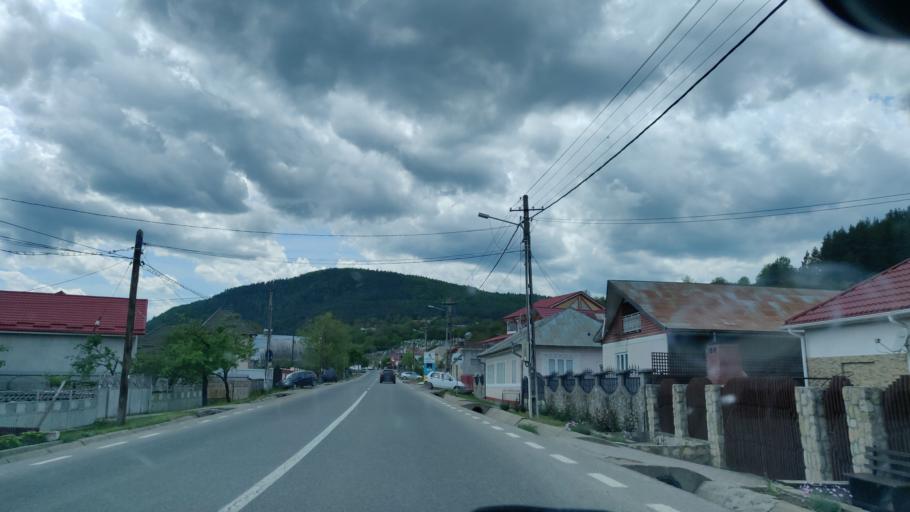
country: RO
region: Vrancea
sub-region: Comuna Tulnici
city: Tulnici
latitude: 45.9242
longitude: 26.6795
